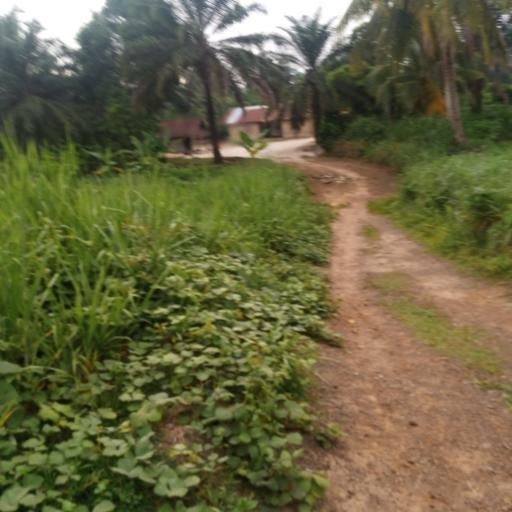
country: SL
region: Eastern Province
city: Pendembu
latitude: 8.0929
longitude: -10.6925
